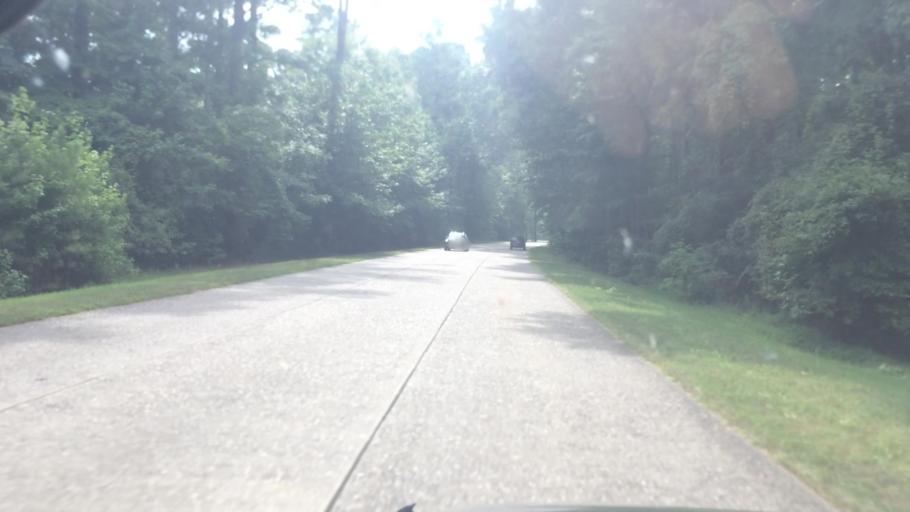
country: US
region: Virginia
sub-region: James City County
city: Williamsburg
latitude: 37.2168
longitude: -76.7533
